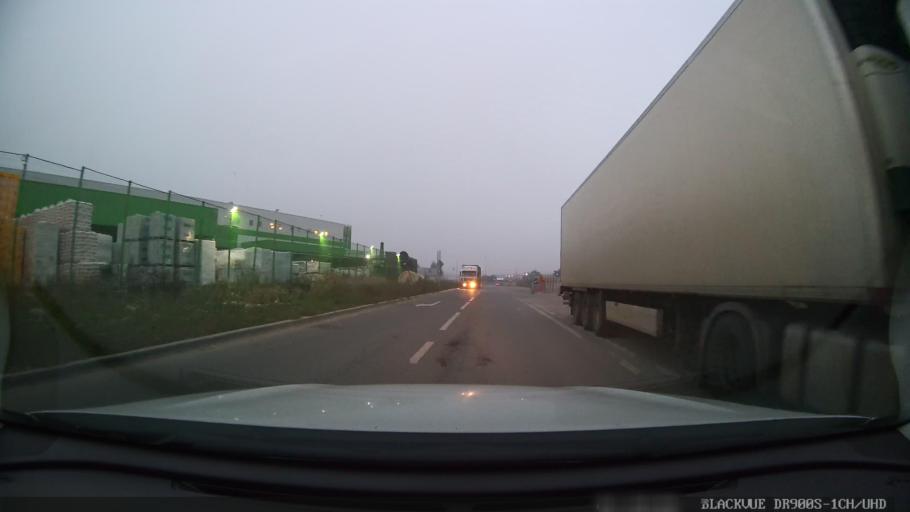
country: RU
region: Moscow
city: Solntsevo
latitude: 55.6202
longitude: 37.3896
